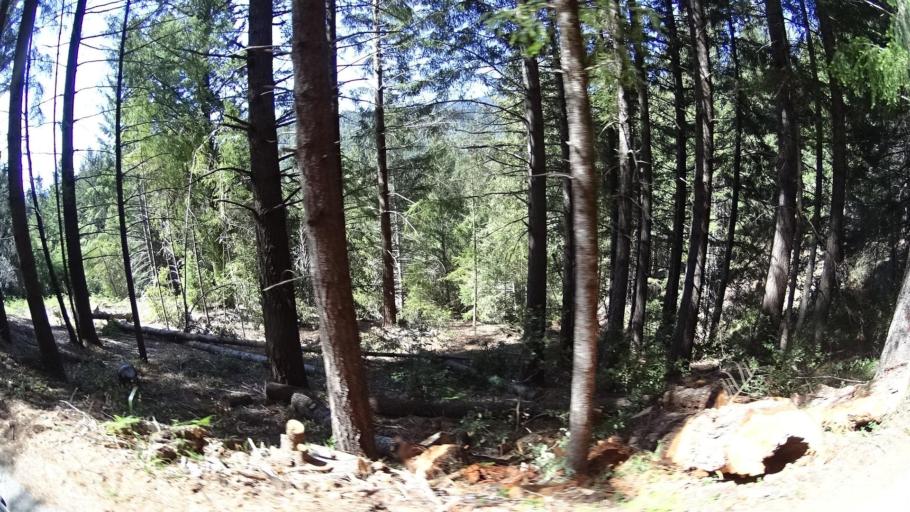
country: US
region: California
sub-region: Humboldt County
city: Redway
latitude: 40.1518
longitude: -124.0363
